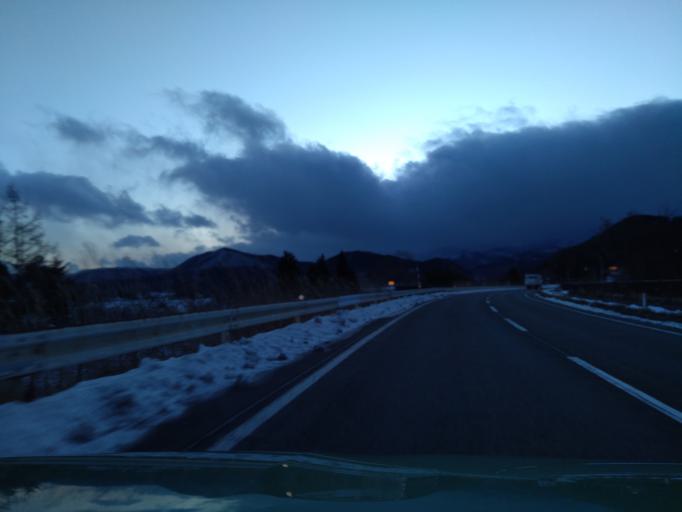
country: JP
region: Iwate
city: Shizukuishi
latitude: 39.6929
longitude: 140.9341
